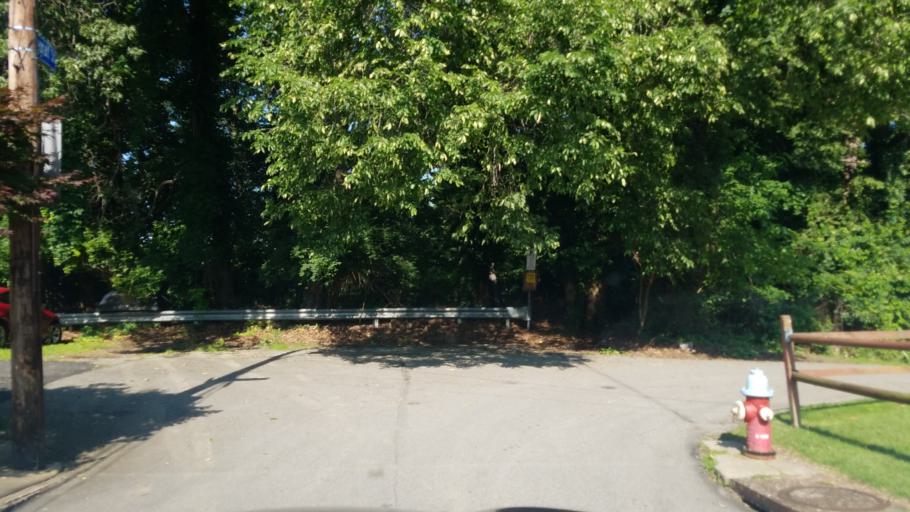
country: US
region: Pennsylvania
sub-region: Allegheny County
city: Homestead
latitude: 40.4208
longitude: -79.9066
